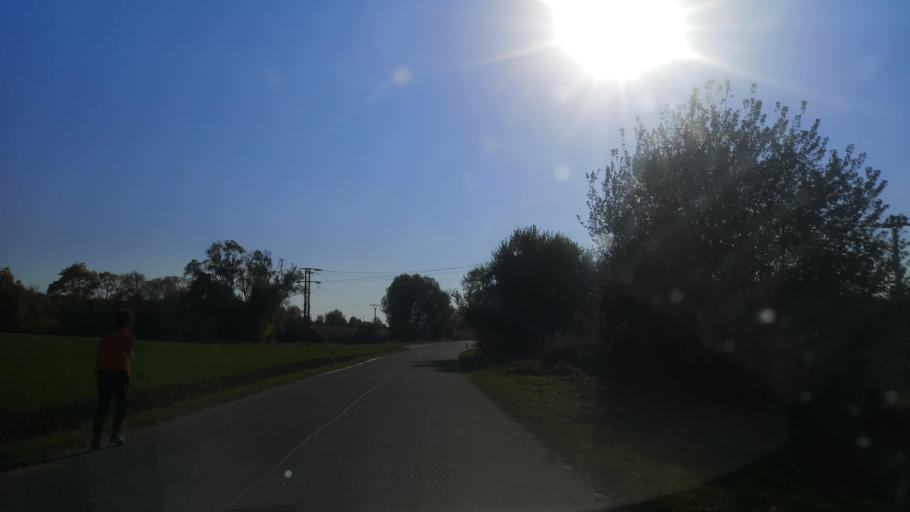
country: SK
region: Nitriansky
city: Zlate Moravce
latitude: 48.4296
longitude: 18.4266
